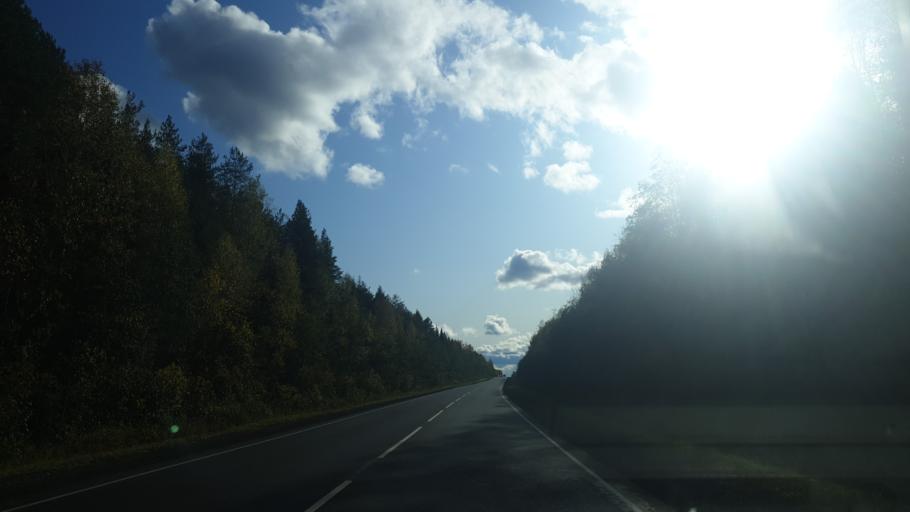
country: RU
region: Komi Republic
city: Letka
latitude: 60.3592
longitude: 49.6723
